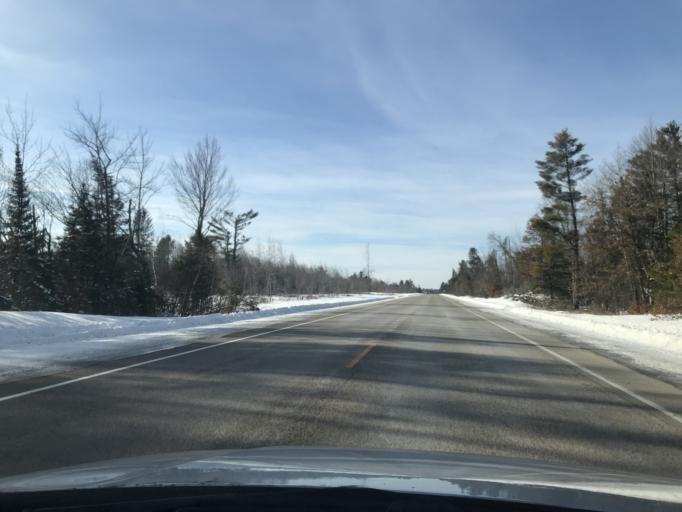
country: US
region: Wisconsin
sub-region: Oconto County
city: Gillett
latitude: 45.1145
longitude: -88.3518
